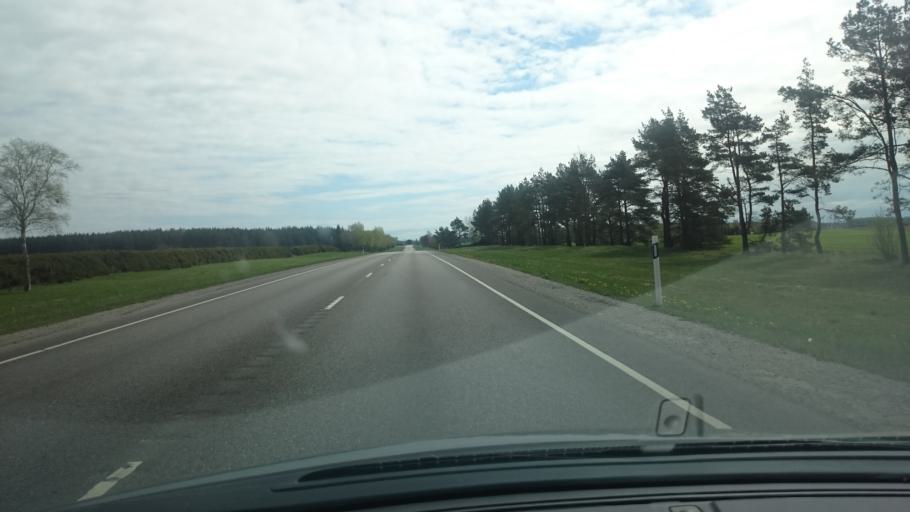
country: EE
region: Laeaene-Virumaa
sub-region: Haljala vald
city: Haljala
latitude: 59.4189
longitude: 26.3155
